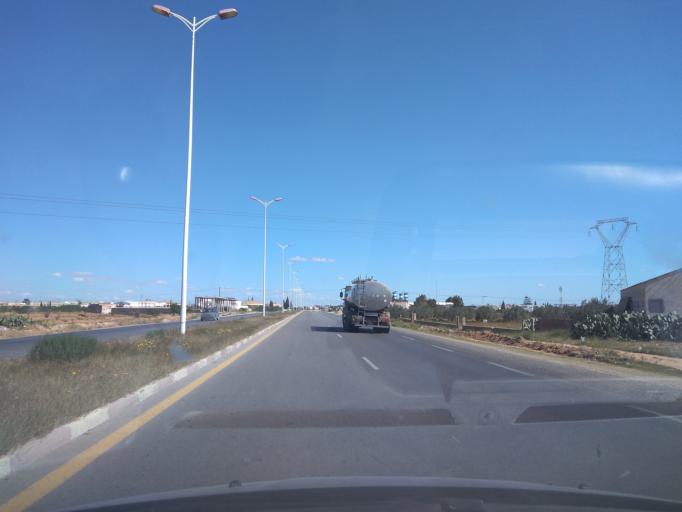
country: TN
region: Safaqis
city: Sfax
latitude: 34.8068
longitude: 10.6916
